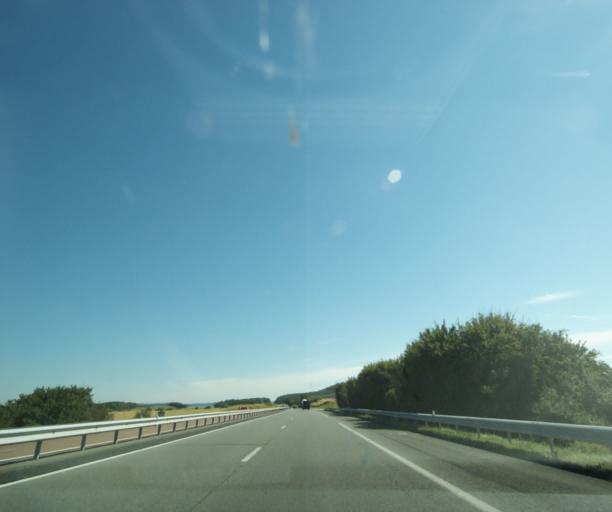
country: FR
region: Champagne-Ardenne
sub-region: Departement de la Haute-Marne
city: Avrecourt
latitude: 48.0483
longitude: 5.5742
